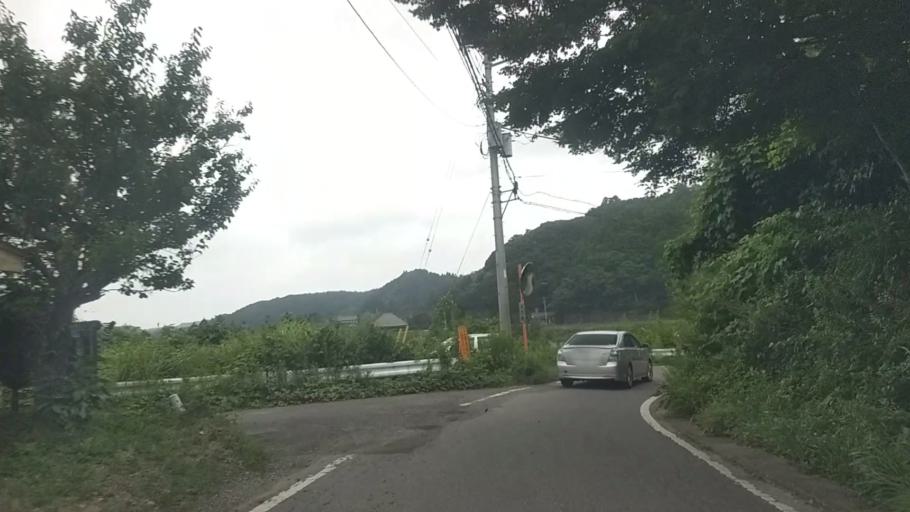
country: JP
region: Chiba
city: Kawaguchi
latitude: 35.2168
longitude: 140.1359
